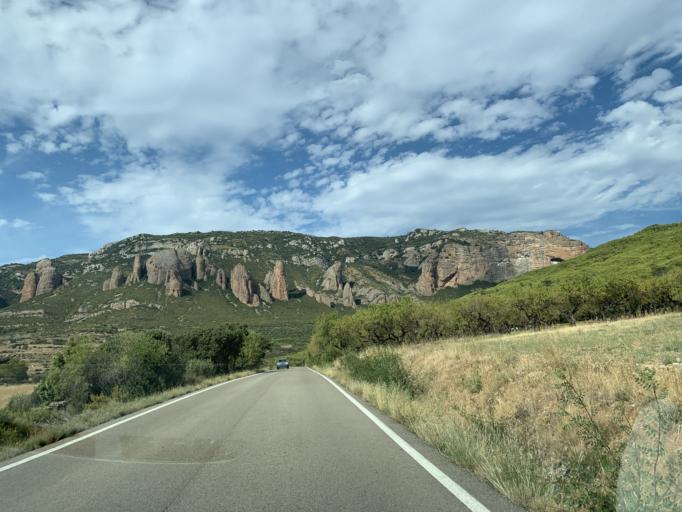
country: ES
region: Aragon
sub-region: Provincia de Zaragoza
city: Santa Eulalia de Gallego
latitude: 42.3336
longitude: -0.7227
